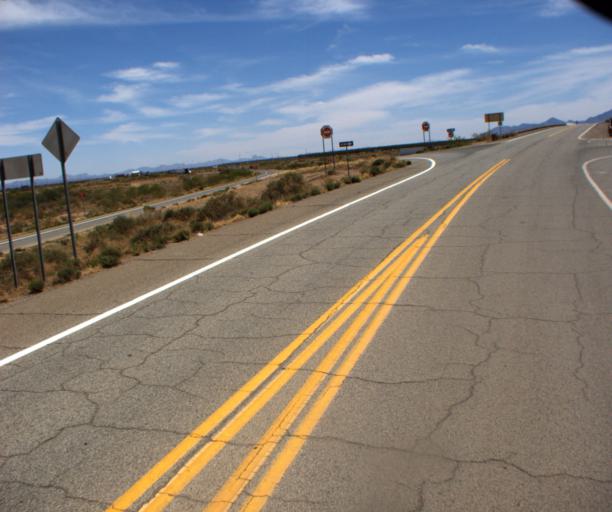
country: US
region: Arizona
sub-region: Cochise County
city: Willcox
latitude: 32.3191
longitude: -109.4510
